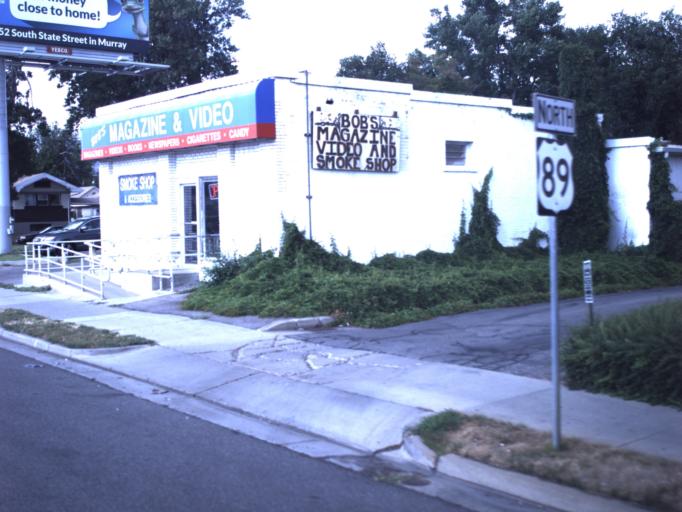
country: US
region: Utah
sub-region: Salt Lake County
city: Salt Lake City
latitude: 40.7424
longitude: -111.8881
